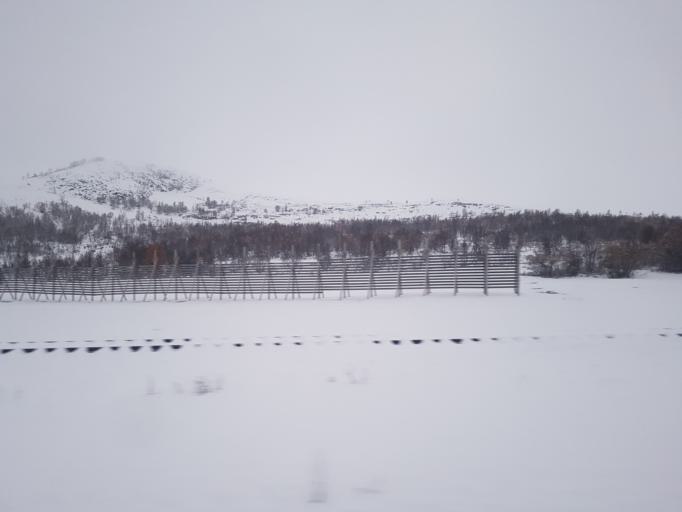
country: NO
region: Oppland
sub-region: Dovre
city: Dovre
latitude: 62.2348
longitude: 9.5363
